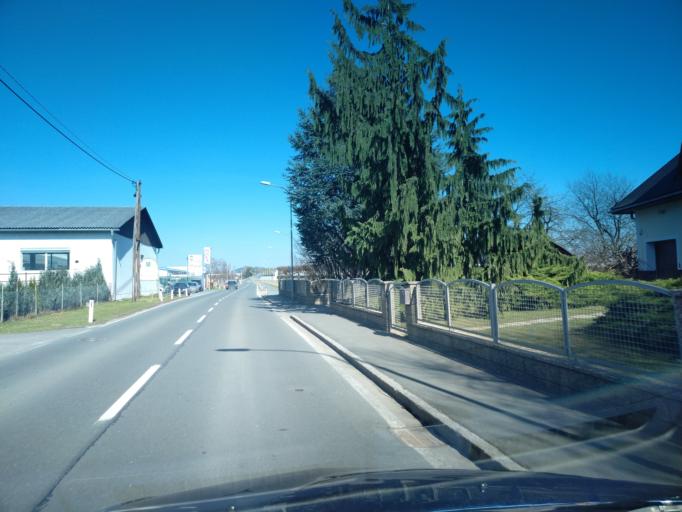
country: AT
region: Styria
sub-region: Politischer Bezirk Graz-Umgebung
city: Wundschuh
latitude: 46.9281
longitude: 15.4542
